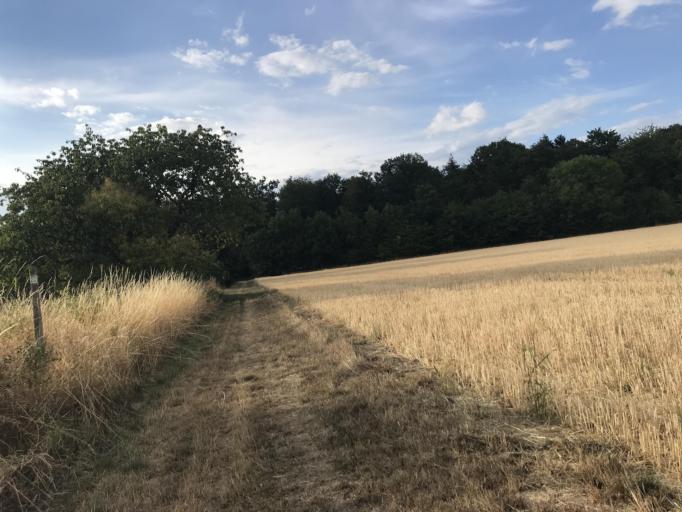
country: DE
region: Rheinland-Pfalz
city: Ober-Olm
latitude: 49.9515
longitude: 8.1852
